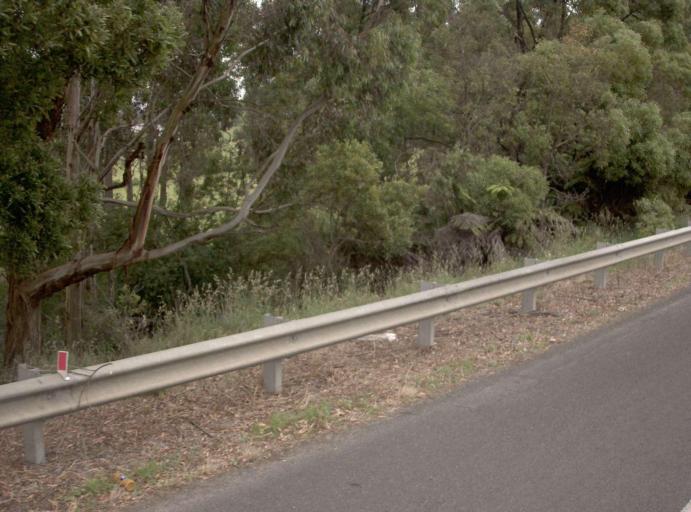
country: AU
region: Victoria
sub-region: Baw Baw
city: Warragul
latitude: -38.1206
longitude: 145.8687
